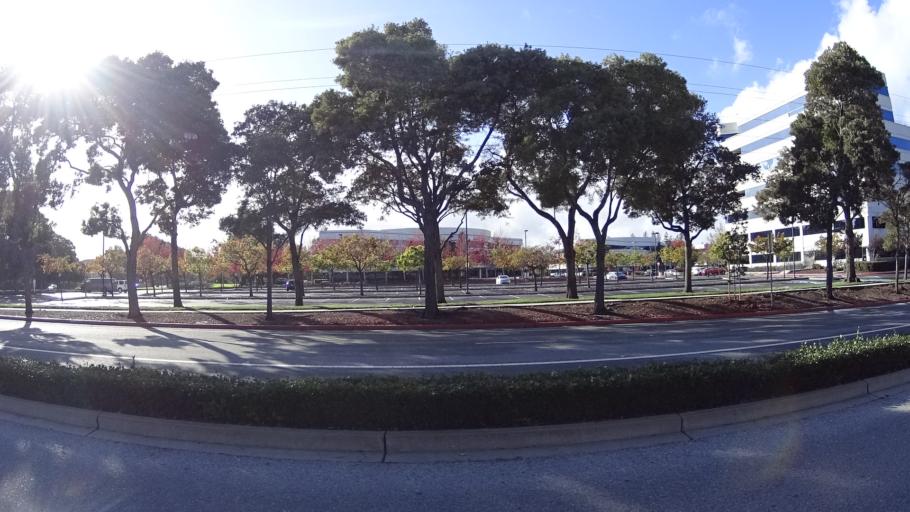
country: US
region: California
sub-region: San Mateo County
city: Foster City
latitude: 37.5560
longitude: -122.2791
